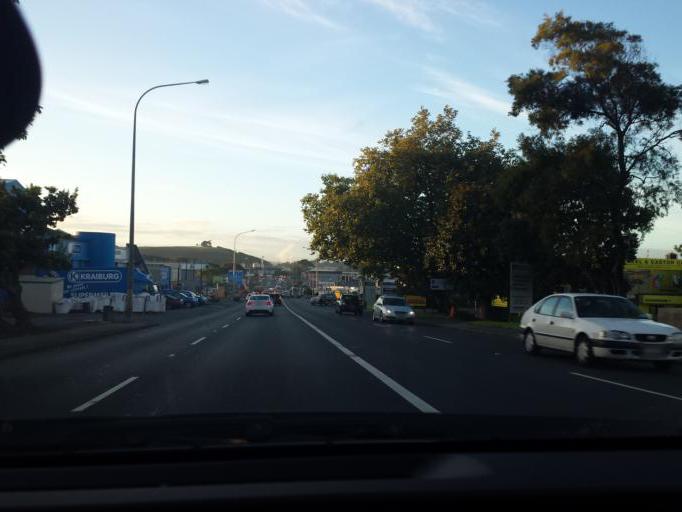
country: NZ
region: Auckland
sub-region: Auckland
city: Tamaki
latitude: -36.9155
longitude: 174.8223
